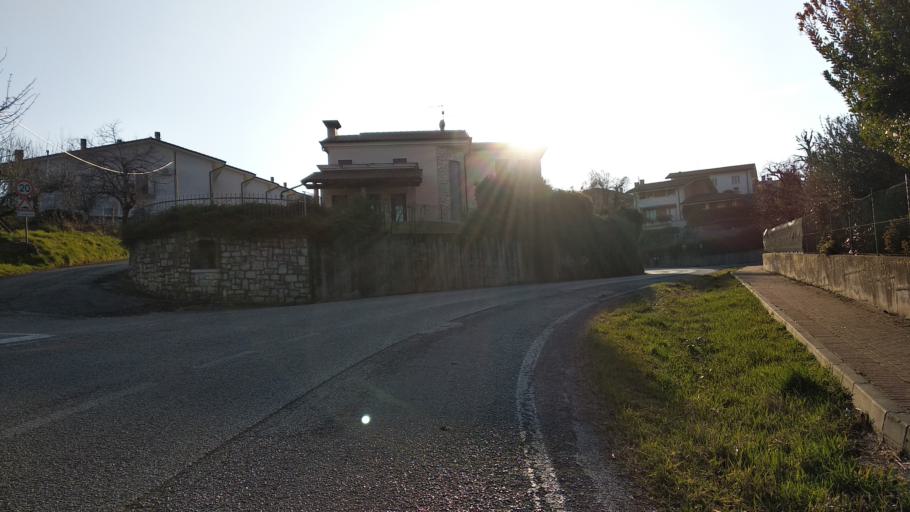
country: IT
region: Veneto
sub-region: Provincia di Vicenza
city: Monte di Malo
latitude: 45.6625
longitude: 11.3646
